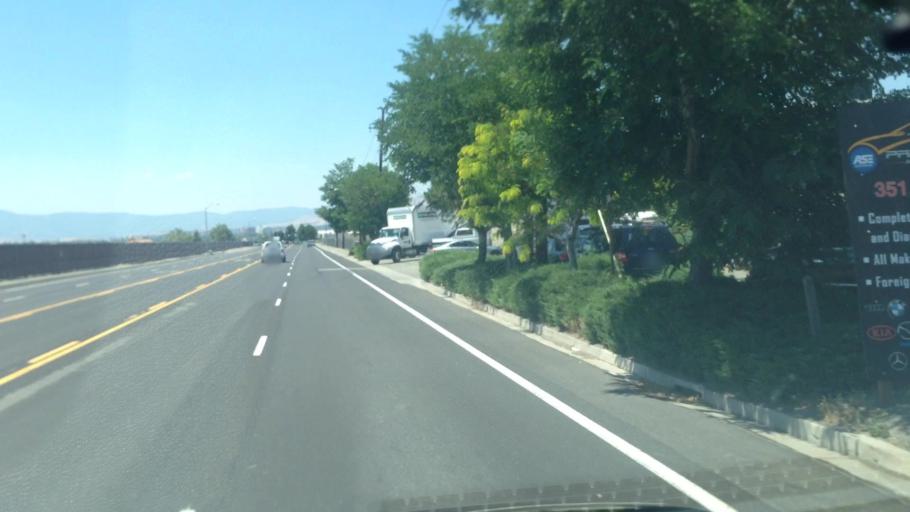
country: US
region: Nevada
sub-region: Washoe County
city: Sparks
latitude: 39.5166
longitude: -119.7639
